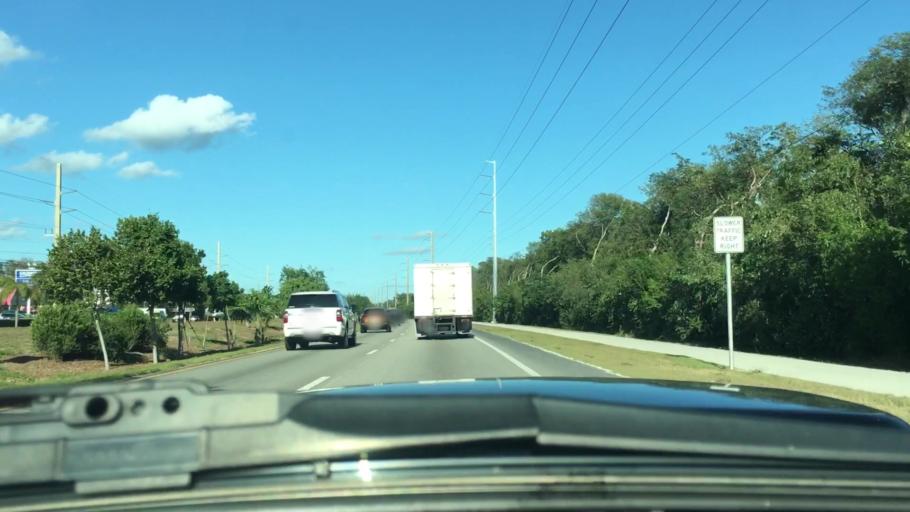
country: US
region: Florida
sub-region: Monroe County
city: Key Largo
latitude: 25.1015
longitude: -80.4328
